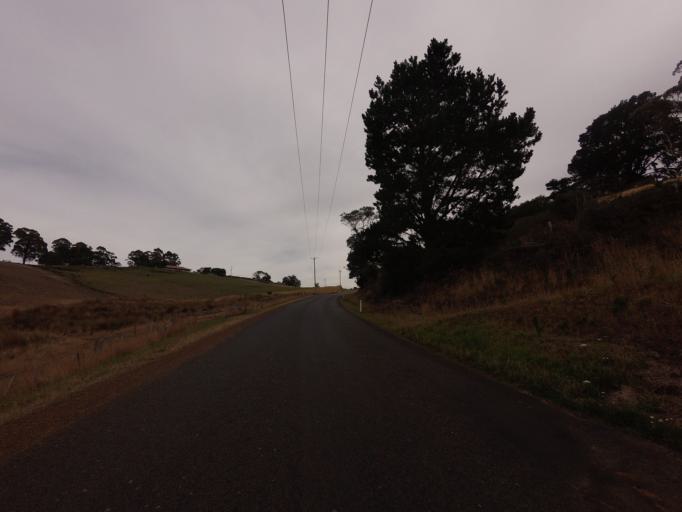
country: AU
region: Tasmania
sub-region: Sorell
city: Sorell
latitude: -42.5332
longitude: 147.5665
